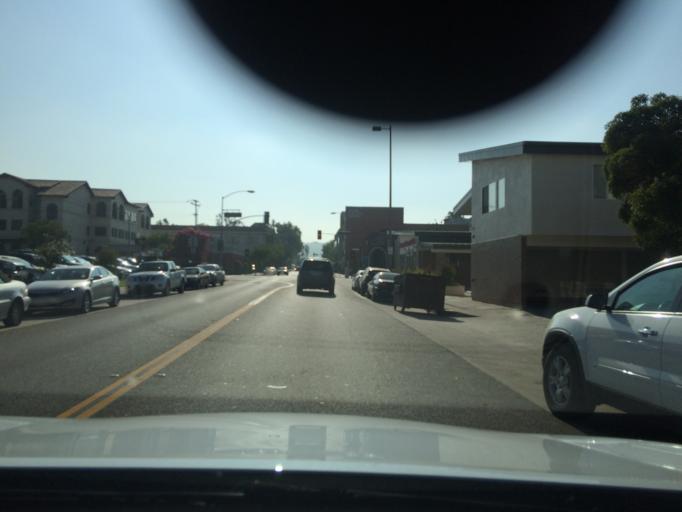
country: US
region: California
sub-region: Los Angeles County
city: Glendale
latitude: 34.1481
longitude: -118.2510
